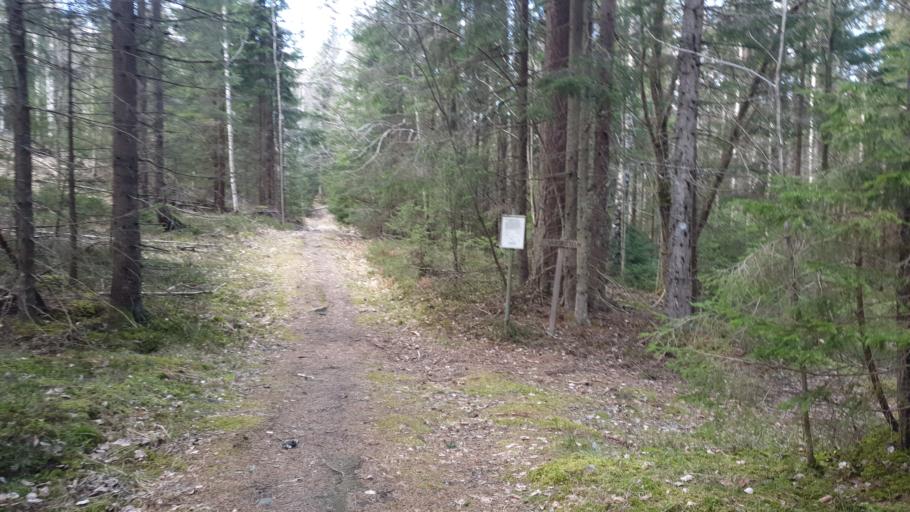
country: SE
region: OErebro
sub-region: Orebro Kommun
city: Garphyttan
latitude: 59.3677
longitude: 14.9753
